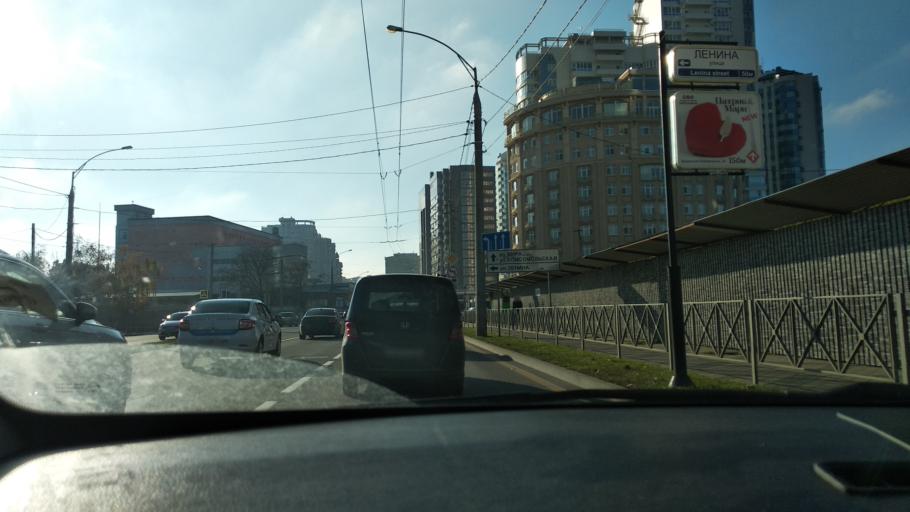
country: RU
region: Krasnodarskiy
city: Krasnodar
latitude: 45.0261
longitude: 38.9597
